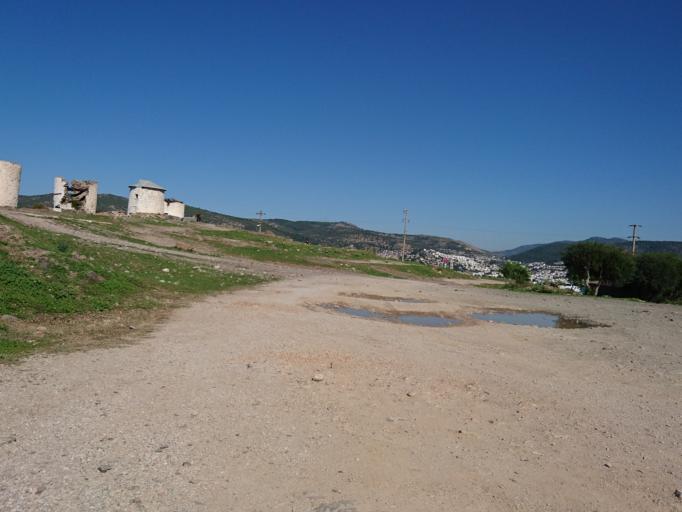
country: TR
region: Mugla
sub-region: Bodrum
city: Bodrum
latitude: 37.0255
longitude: 27.4139
